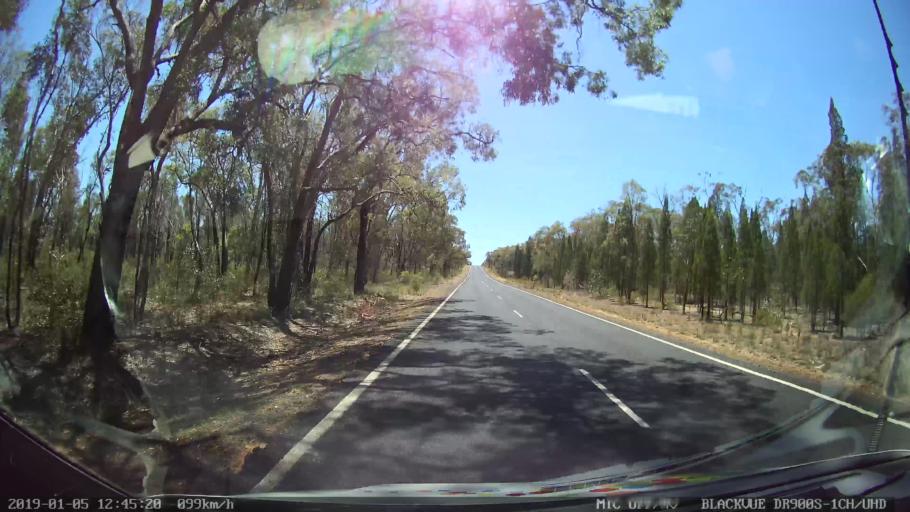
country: AU
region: New South Wales
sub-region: Warrumbungle Shire
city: Coonabarabran
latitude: -31.1287
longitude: 149.5488
